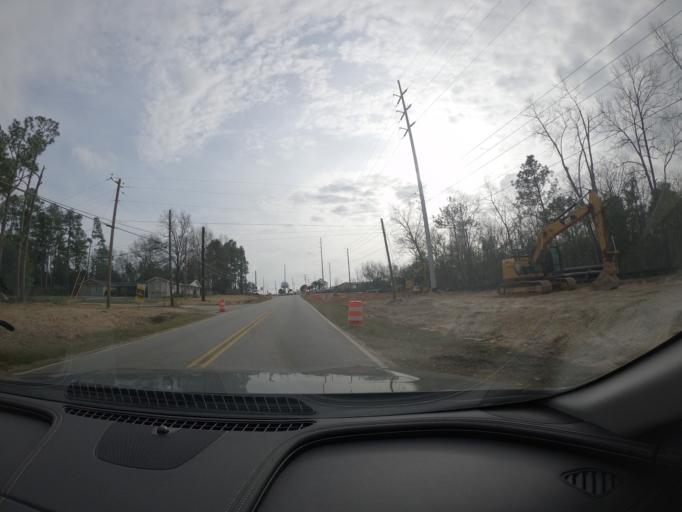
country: US
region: Georgia
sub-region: Columbia County
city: Martinez
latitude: 33.4931
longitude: -82.1098
